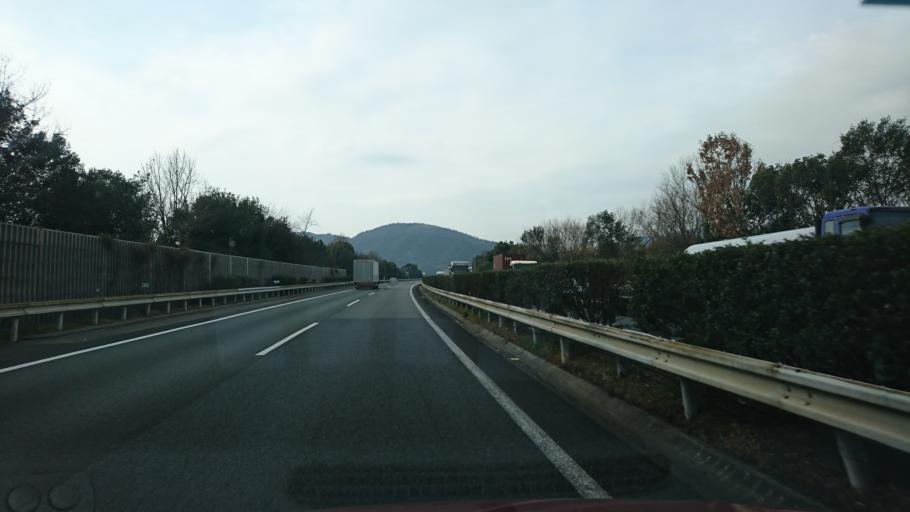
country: JP
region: Okayama
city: Kamogatacho-kamogata
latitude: 34.5396
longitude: 133.5643
